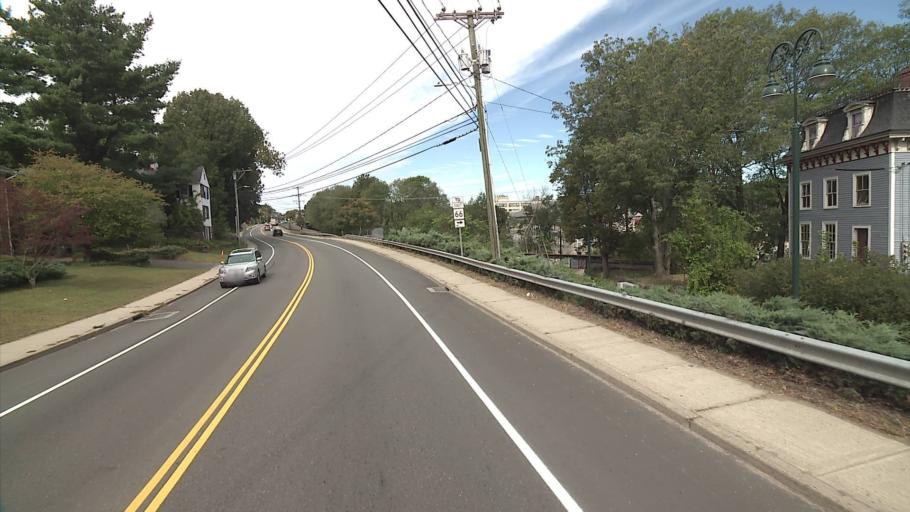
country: US
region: Connecticut
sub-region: Windham County
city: Willimantic
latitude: 41.7088
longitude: -72.2056
